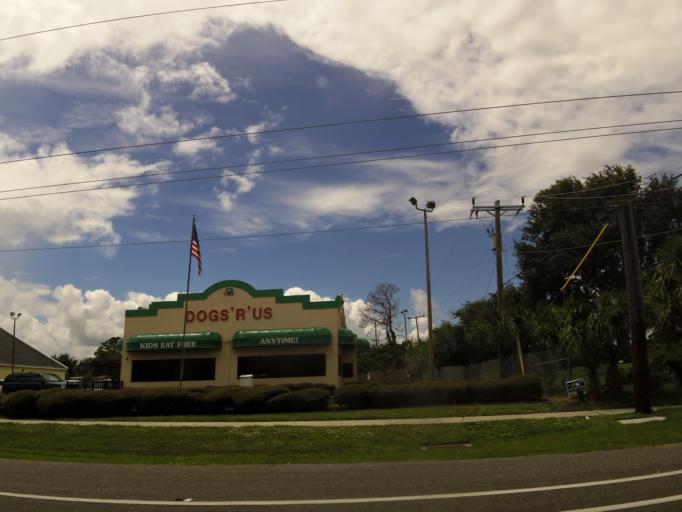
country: US
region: Florida
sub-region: Brevard County
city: Port Saint John
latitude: 28.4812
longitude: -80.7708
